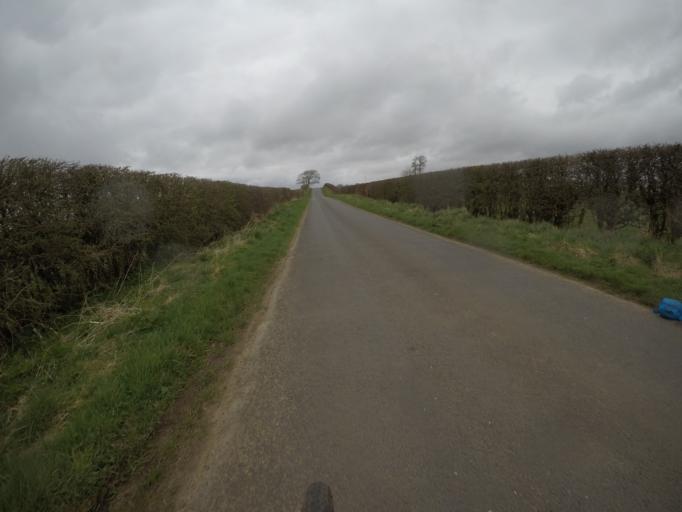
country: GB
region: Scotland
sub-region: East Ayrshire
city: Galston
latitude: 55.6183
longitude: -4.4349
